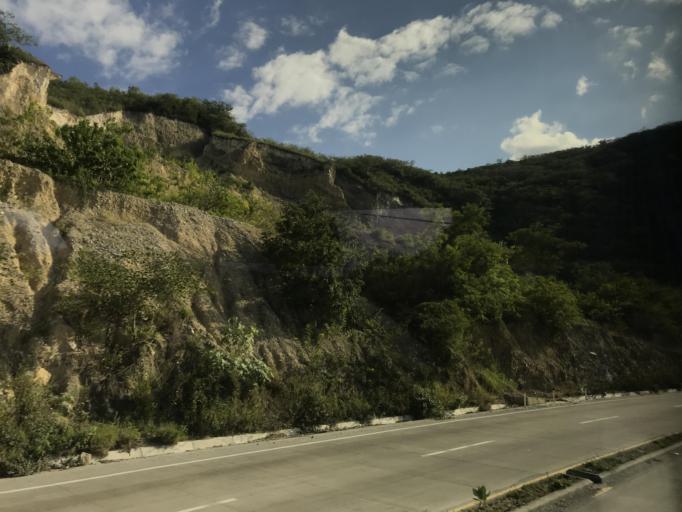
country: GT
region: El Progreso
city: Guastatoya
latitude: 14.8476
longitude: -90.1221
